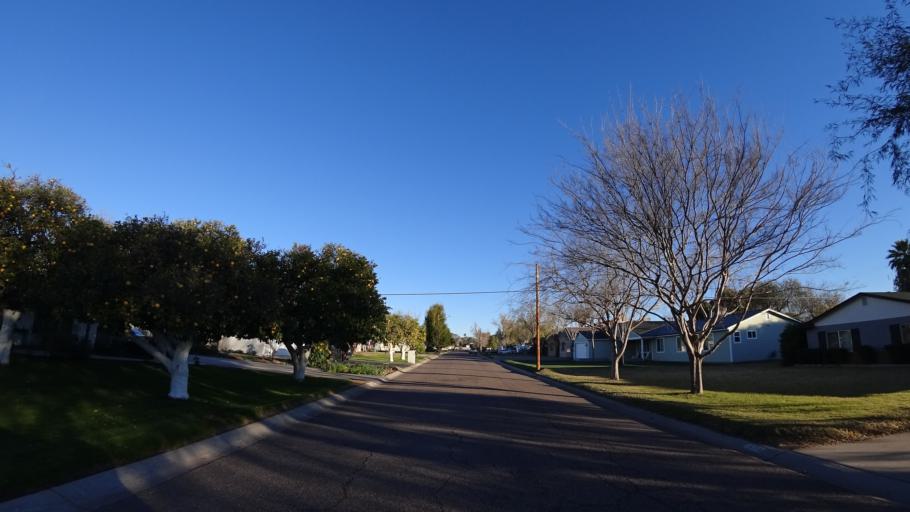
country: US
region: Arizona
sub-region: Maricopa County
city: Paradise Valley
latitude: 33.4895
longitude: -112.0075
